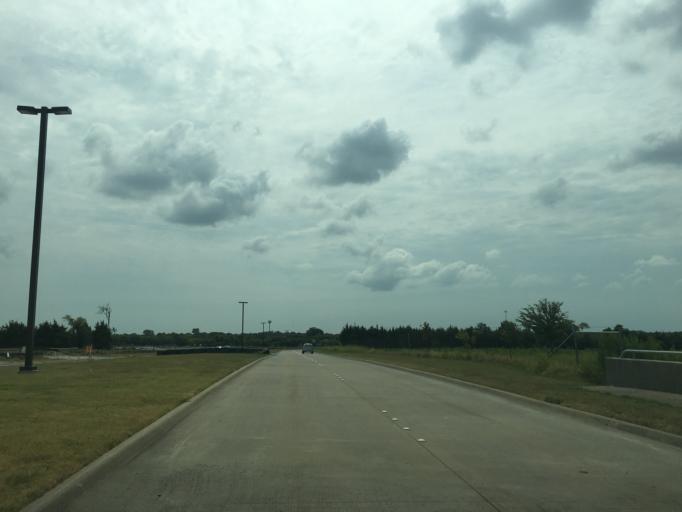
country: US
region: Texas
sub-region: Rockwall County
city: Rockwall
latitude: 32.9565
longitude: -96.4481
